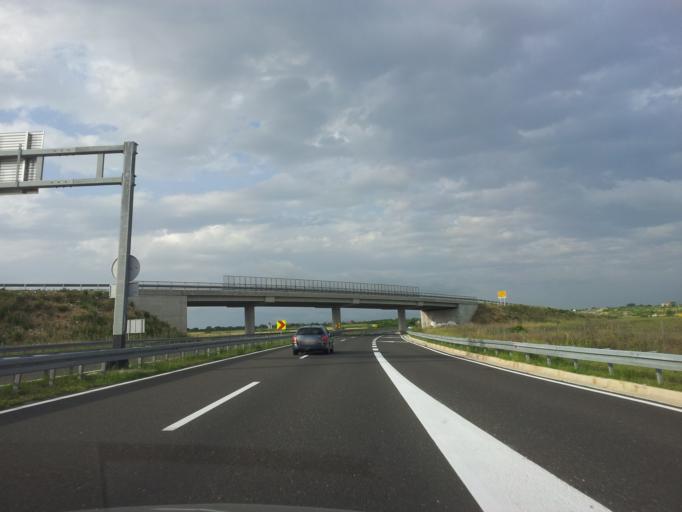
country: HR
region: Zadarska
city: Galovac
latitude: 44.1123
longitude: 15.4019
